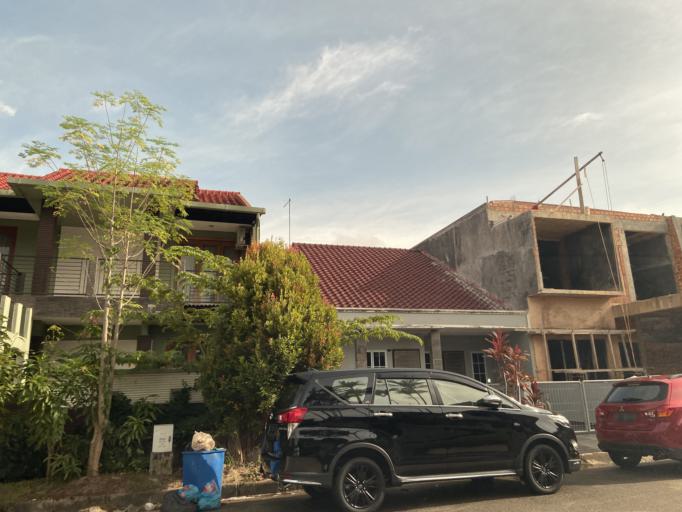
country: SG
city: Singapore
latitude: 1.1135
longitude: 104.0223
